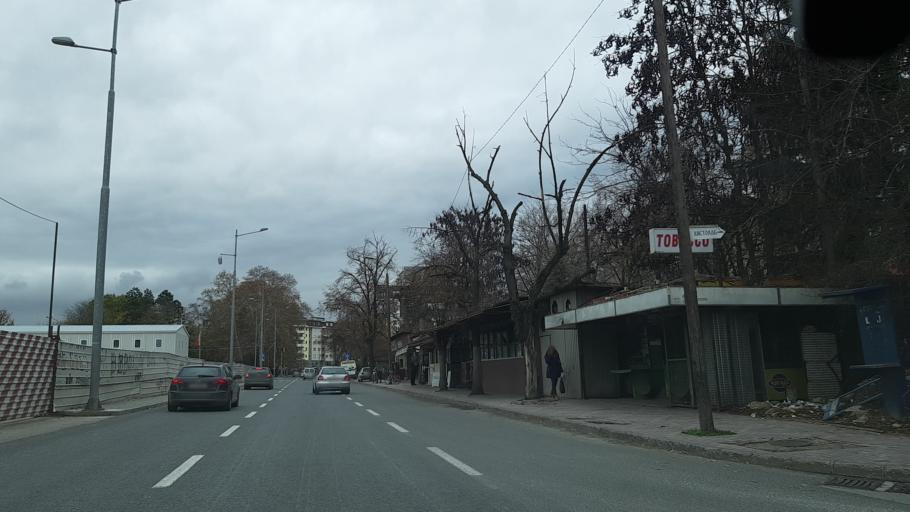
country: MK
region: Karpos
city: Skopje
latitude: 41.9895
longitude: 21.4292
